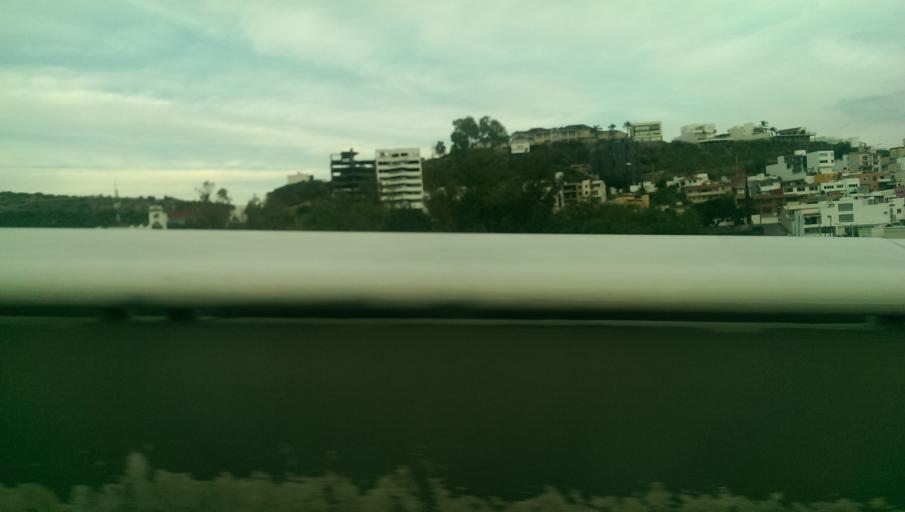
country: MX
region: Queretaro
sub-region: Queretaro
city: Santiago de Queretaro
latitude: 20.5875
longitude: -100.3633
